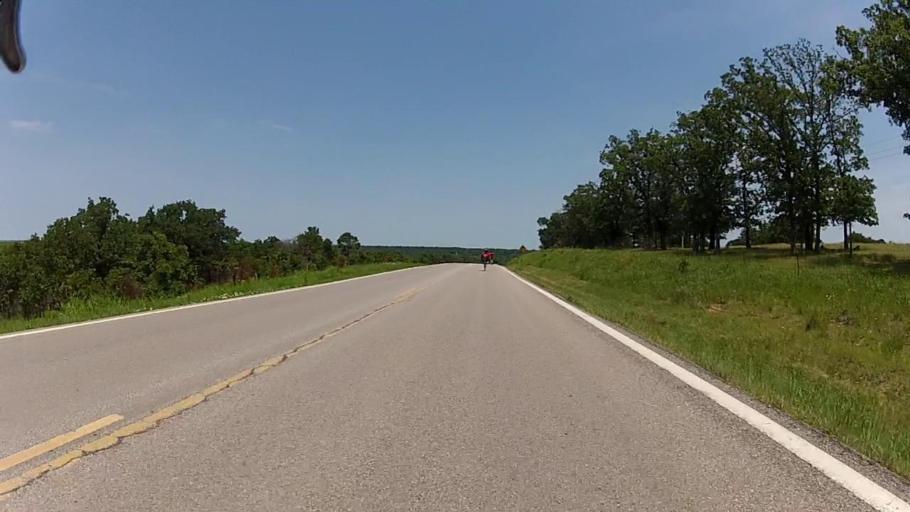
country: US
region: Kansas
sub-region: Chautauqua County
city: Sedan
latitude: 37.1179
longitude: -96.2377
